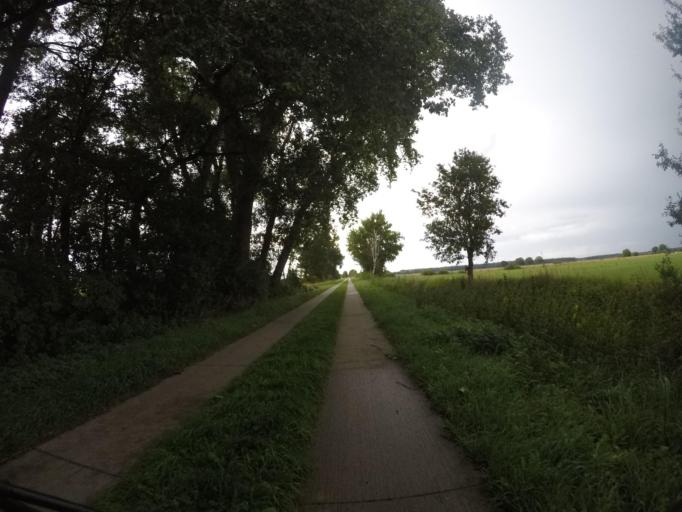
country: DE
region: Lower Saxony
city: Neu Darchau
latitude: 53.2541
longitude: 10.8827
